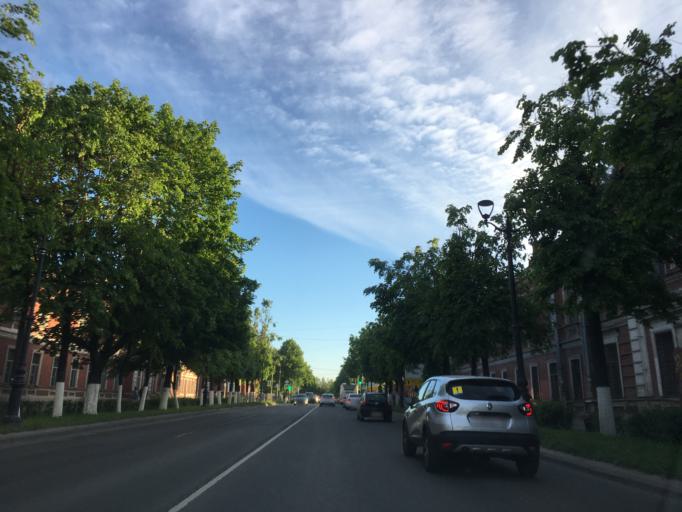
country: RU
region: Leningrad
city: Gatchina
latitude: 59.5760
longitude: 30.1310
